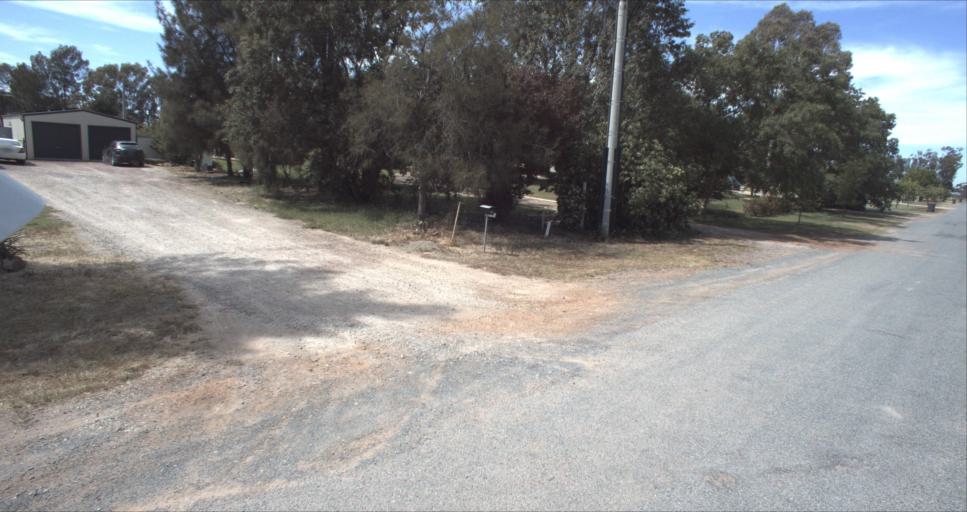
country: AU
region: New South Wales
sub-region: Leeton
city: Leeton
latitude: -34.5614
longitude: 146.4187
